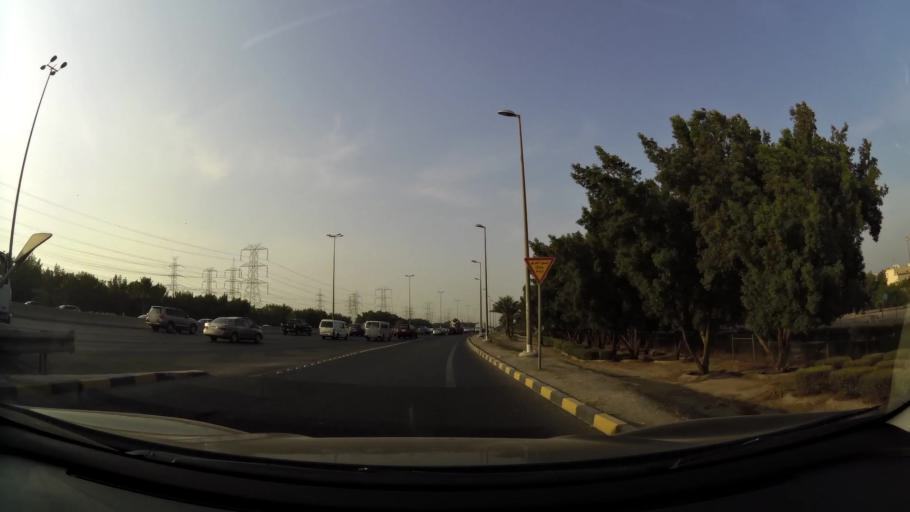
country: KW
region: Mubarak al Kabir
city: Sabah as Salim
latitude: 29.2221
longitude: 48.0553
